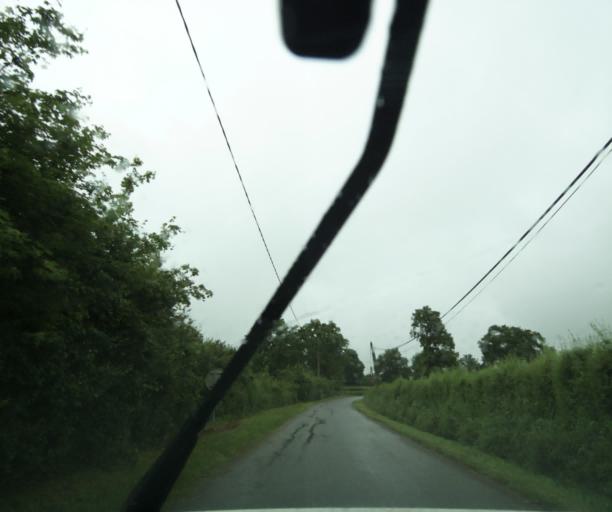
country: FR
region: Bourgogne
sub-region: Departement de Saone-et-Loire
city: Charolles
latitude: 46.4346
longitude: 4.3414
